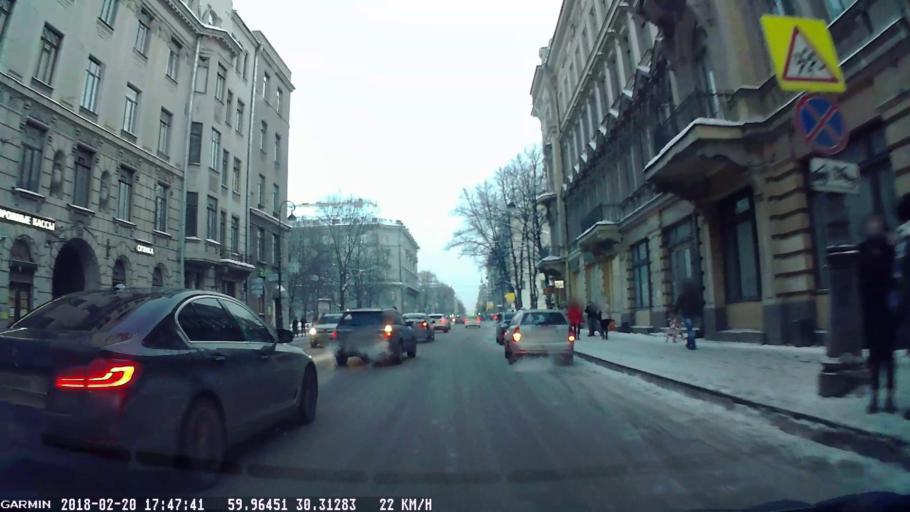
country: RU
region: St.-Petersburg
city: Petrogradka
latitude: 59.9643
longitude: 30.3130
